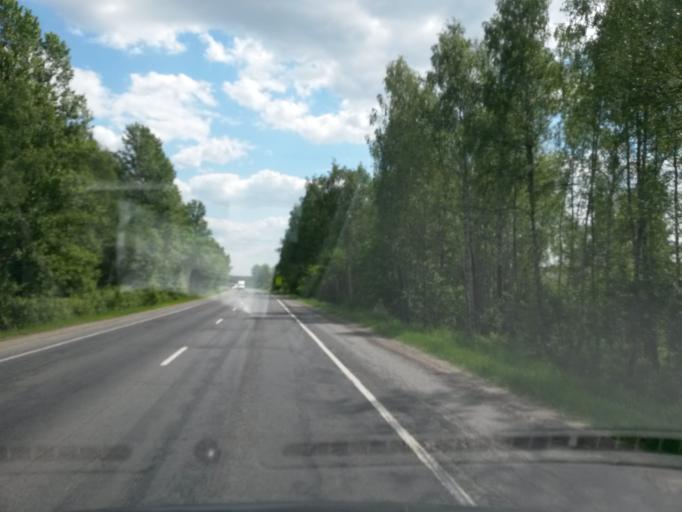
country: RU
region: Jaroslavl
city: Yaroslavl
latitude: 57.5533
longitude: 39.8807
